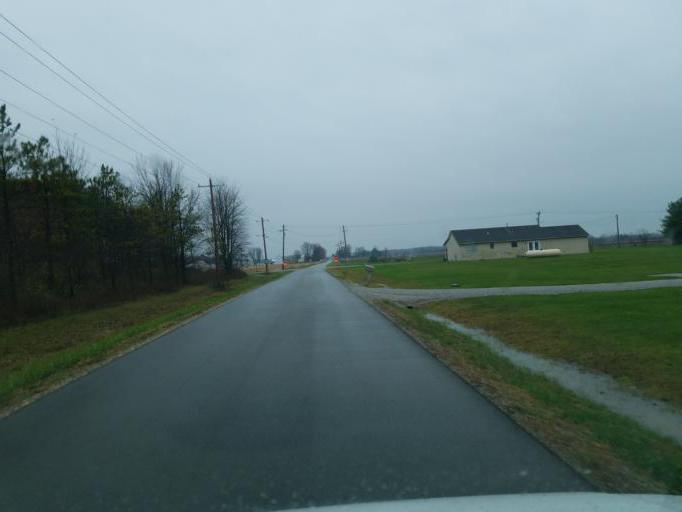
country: US
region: Ohio
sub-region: Knox County
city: Centerburg
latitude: 40.2615
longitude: -82.7359
